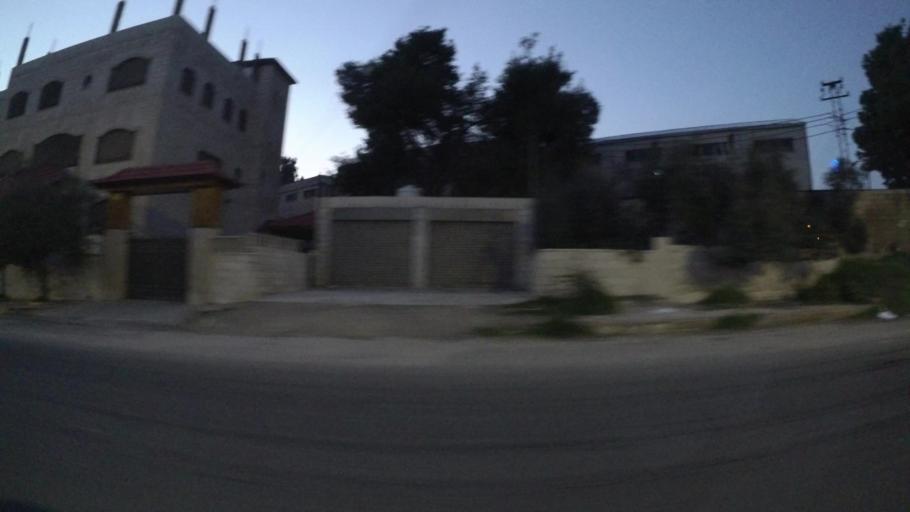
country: JO
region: Amman
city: Al Bunayyat ash Shamaliyah
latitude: 31.8905
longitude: 35.9259
